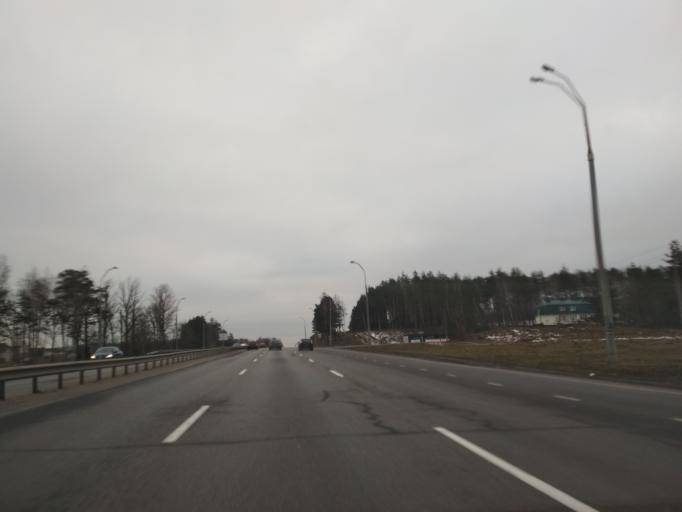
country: BY
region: Minsk
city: Pryvol'ny
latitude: 53.8205
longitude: 27.7624
